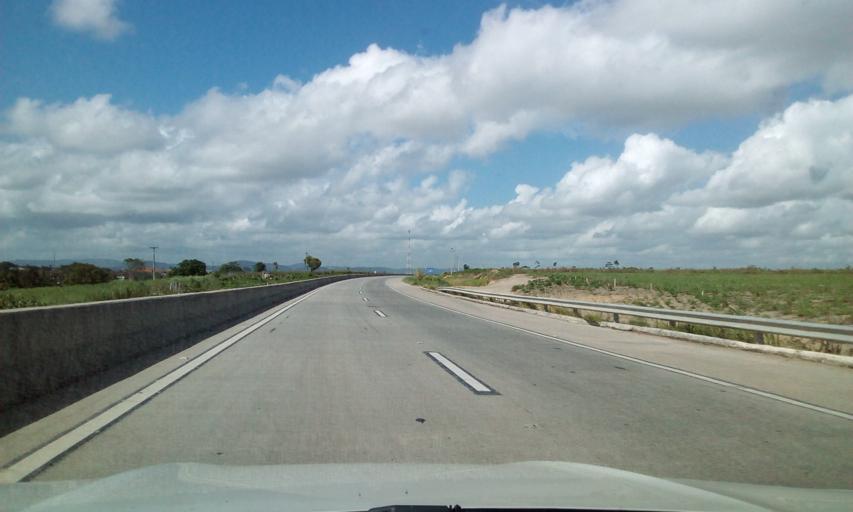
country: BR
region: Alagoas
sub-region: Messias
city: Messias
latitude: -9.3944
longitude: -35.8363
